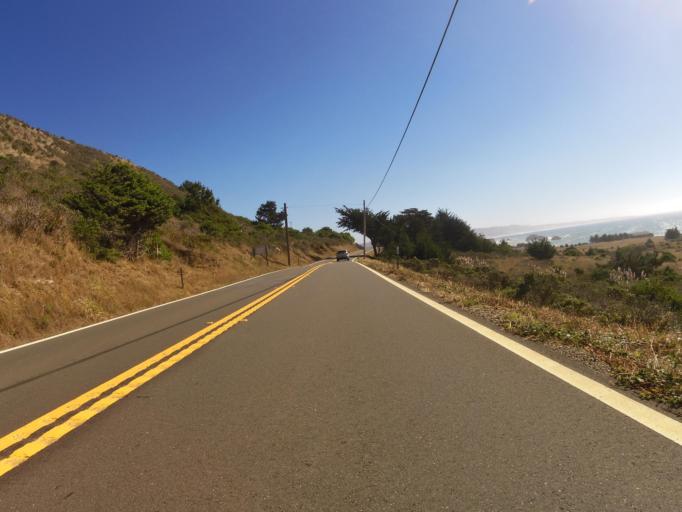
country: US
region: California
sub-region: Mendocino County
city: Fort Bragg
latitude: 39.5964
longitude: -123.7828
